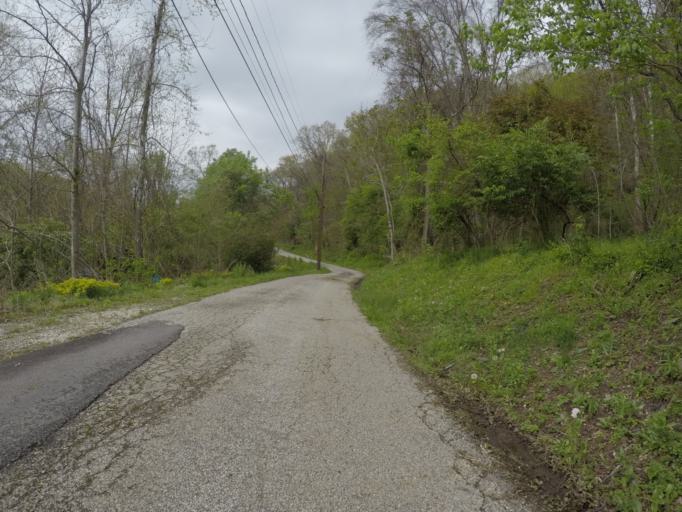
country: US
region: West Virginia
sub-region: Cabell County
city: Huntington
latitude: 38.3941
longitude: -82.4850
